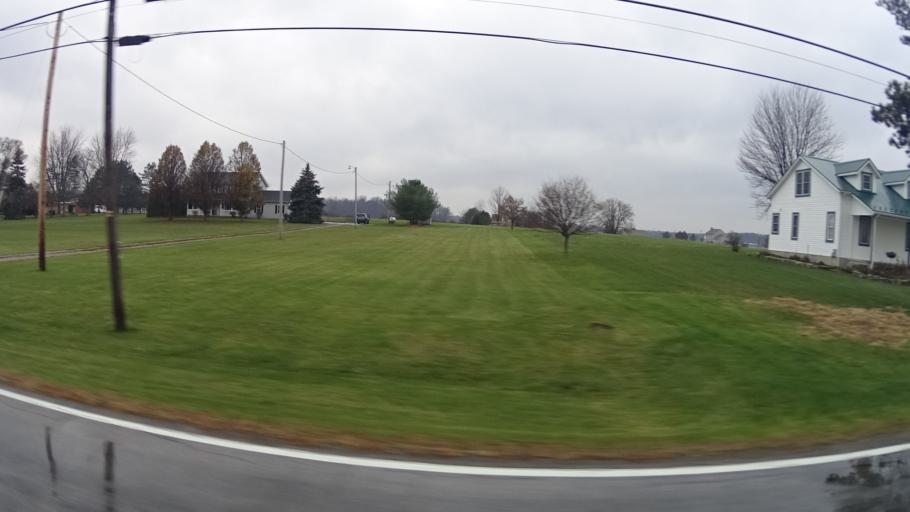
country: US
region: Ohio
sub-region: Lorain County
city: Lagrange
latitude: 41.2727
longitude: -82.1387
